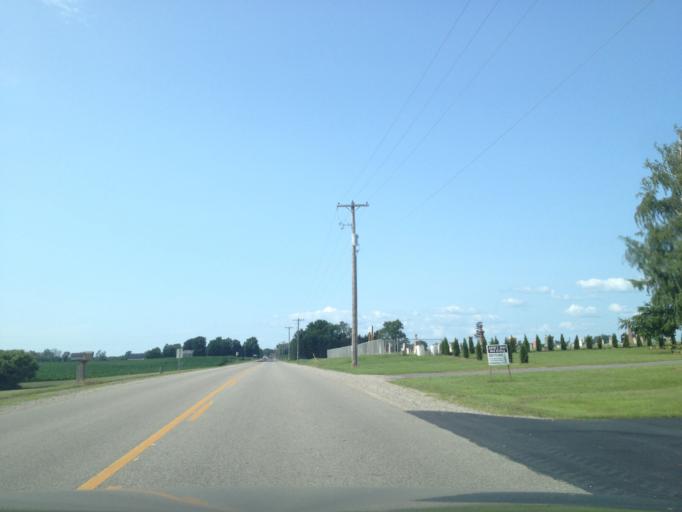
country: CA
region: Ontario
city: Aylmer
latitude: 42.7155
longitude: -80.8589
